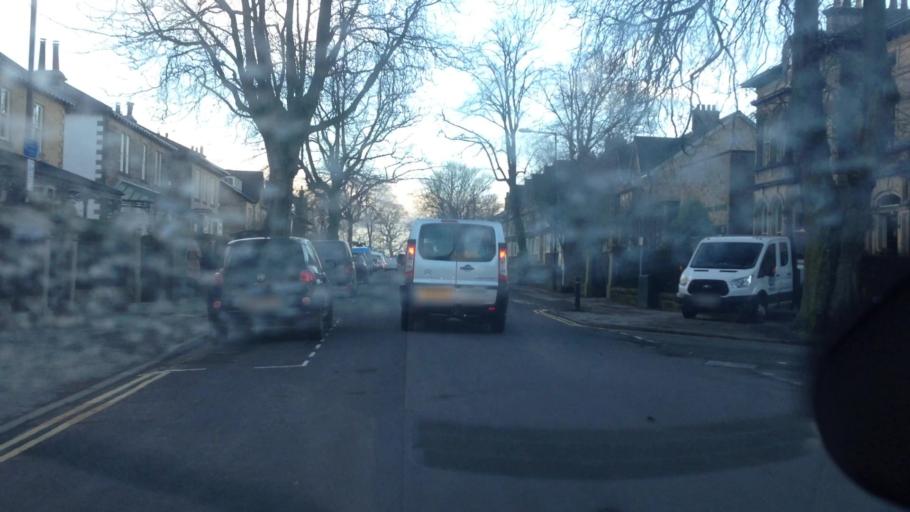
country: GB
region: England
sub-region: North Yorkshire
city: Harrogate
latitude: 53.9917
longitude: -1.5319
